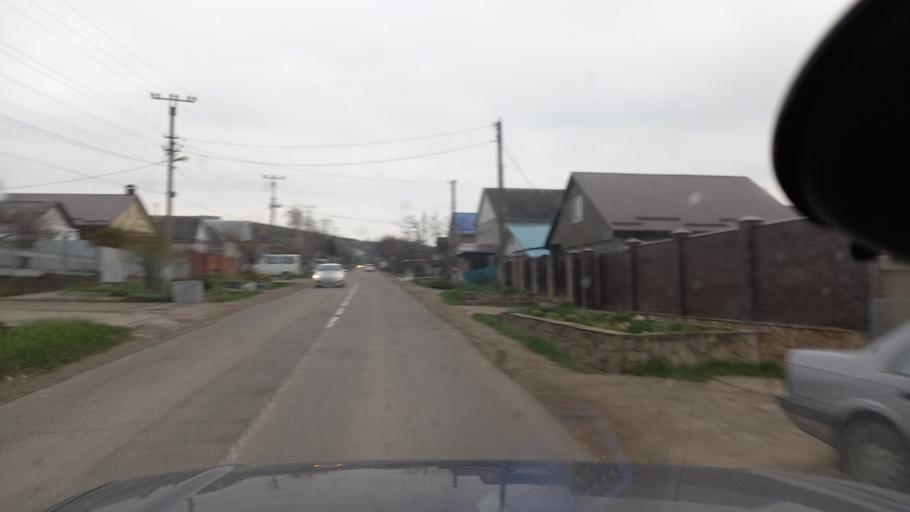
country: RU
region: Krasnodarskiy
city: Sukko
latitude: 44.8521
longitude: 37.4365
